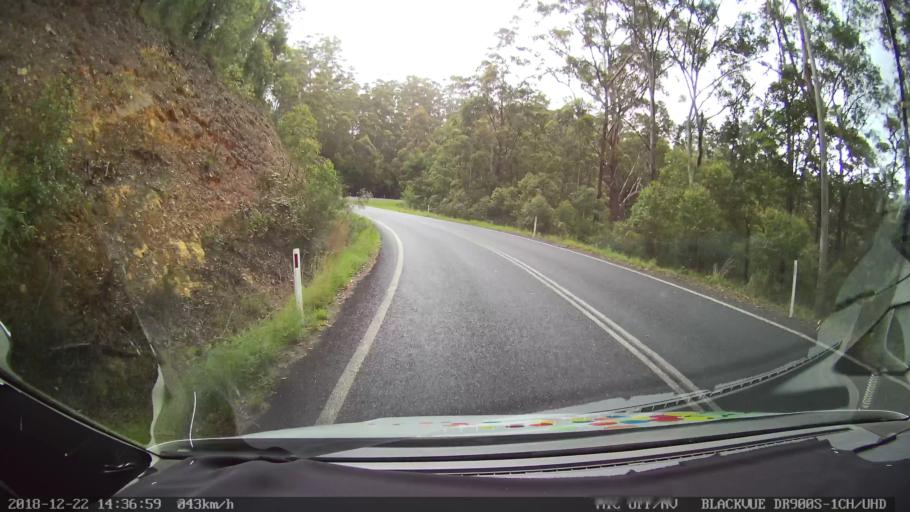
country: AU
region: New South Wales
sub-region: Bellingen
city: Dorrigo
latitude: -30.1314
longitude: 152.6033
